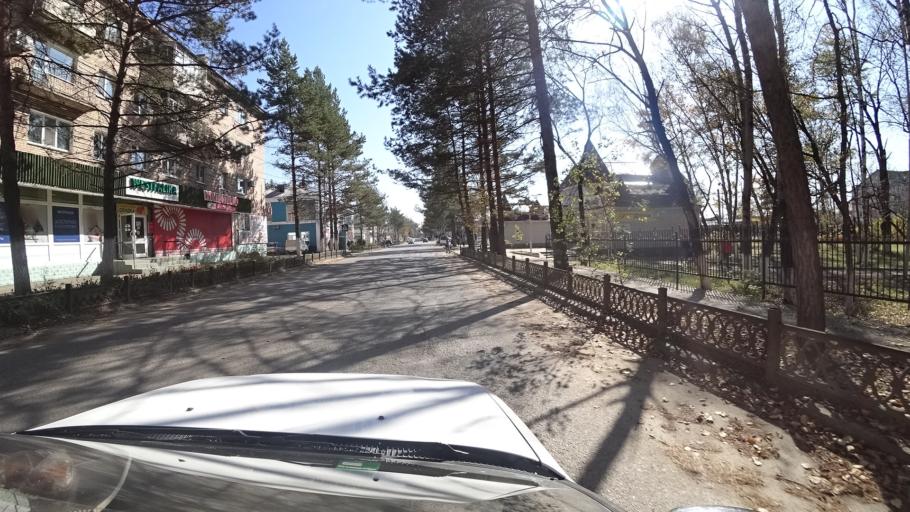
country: RU
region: Primorskiy
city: Dal'nerechensk
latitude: 45.9311
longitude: 133.7310
